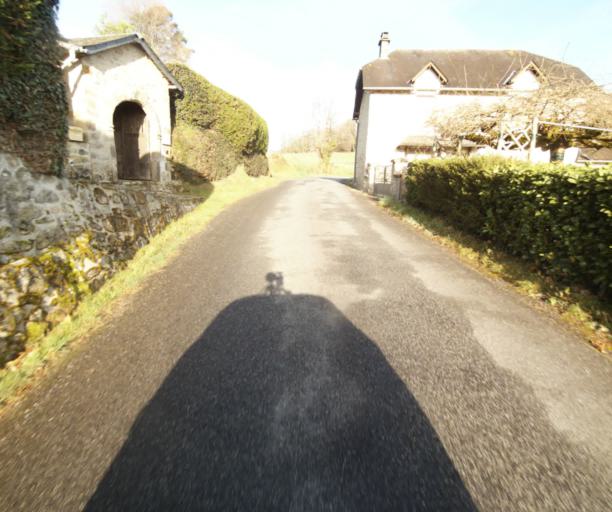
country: FR
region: Limousin
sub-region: Departement de la Correze
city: Correze
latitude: 45.3029
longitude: 1.8491
